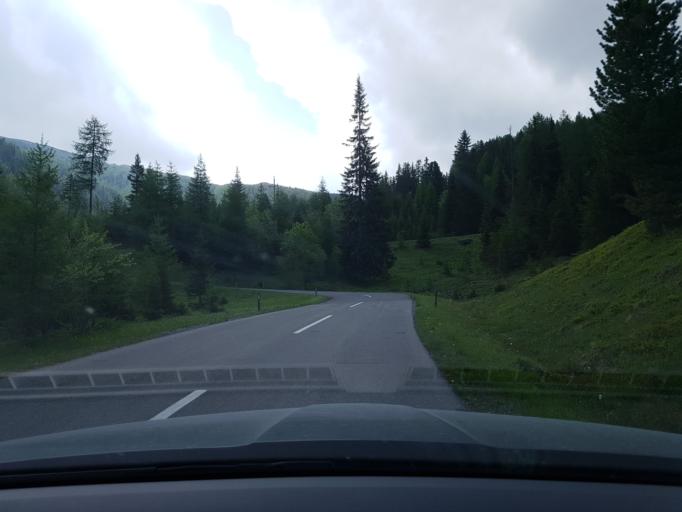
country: AT
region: Salzburg
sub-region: Politischer Bezirk Tamsweg
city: Thomatal
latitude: 46.9553
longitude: 13.7279
